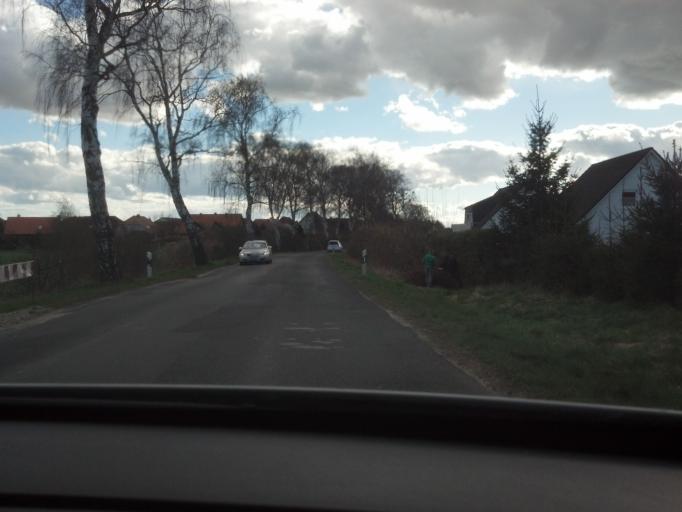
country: DE
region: Mecklenburg-Vorpommern
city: Burg Stargard
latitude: 53.5020
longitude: 13.3216
